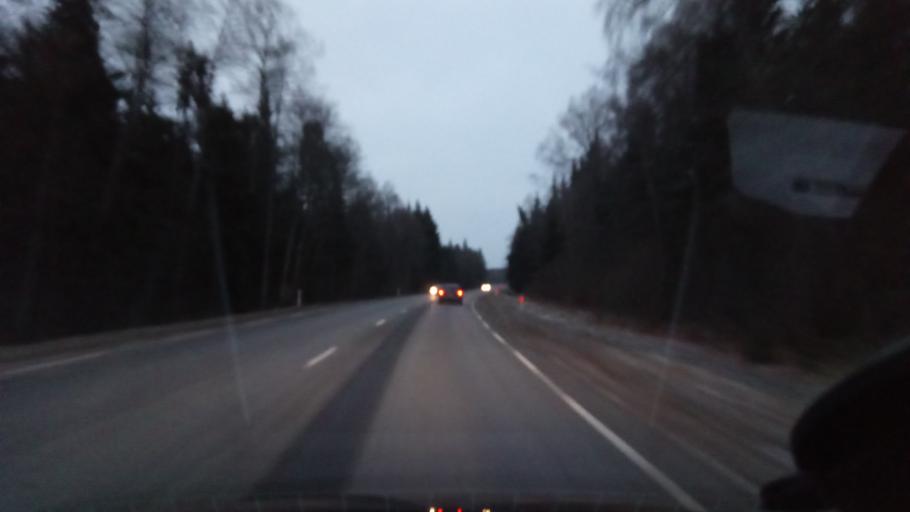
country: LT
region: Vilnius County
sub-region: Trakai
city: Rudiskes
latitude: 54.4329
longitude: 24.9808
